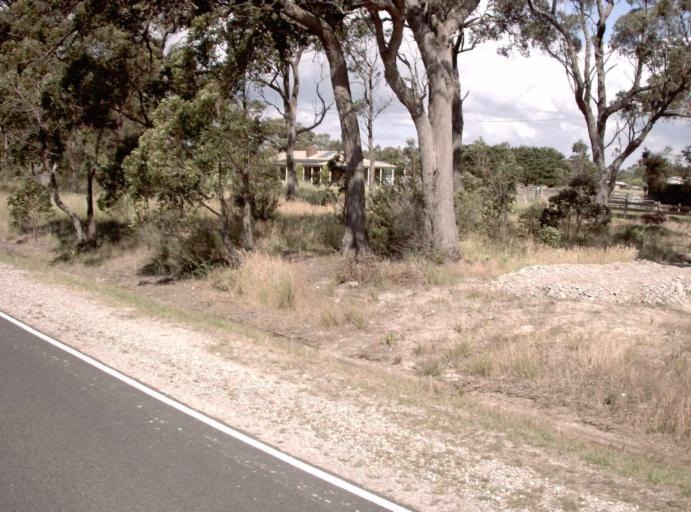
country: AU
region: Victoria
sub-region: Latrobe
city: Traralgon
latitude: -38.1348
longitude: 146.5465
